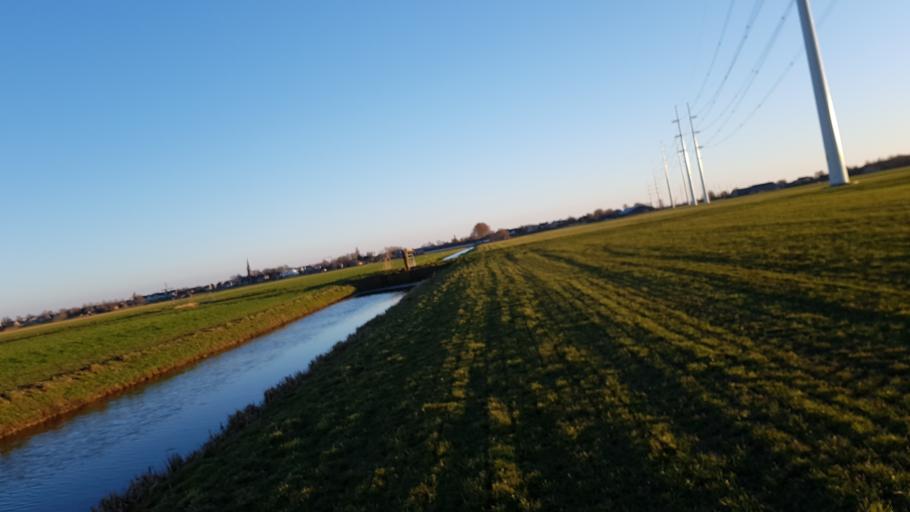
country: NL
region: South Holland
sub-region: Gemeente Rijnwoude
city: Benthuizen
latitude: 52.1059
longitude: 4.5760
